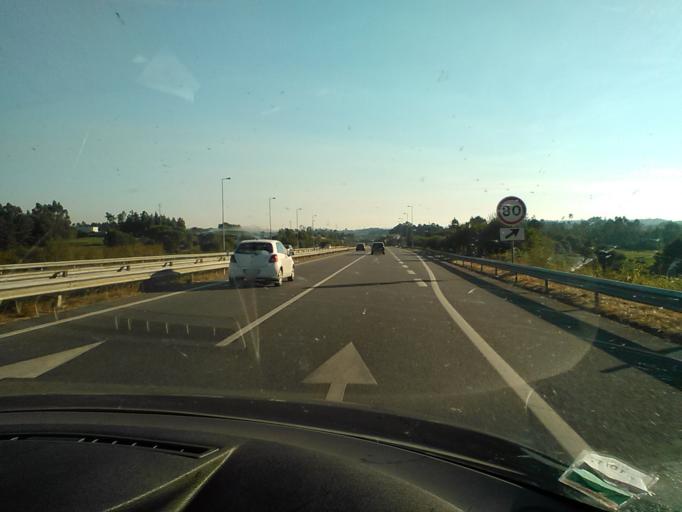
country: PT
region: Braga
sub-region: Vila Nova de Famalicao
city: Vila Nova de Famalicao
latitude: 41.3928
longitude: -8.4761
